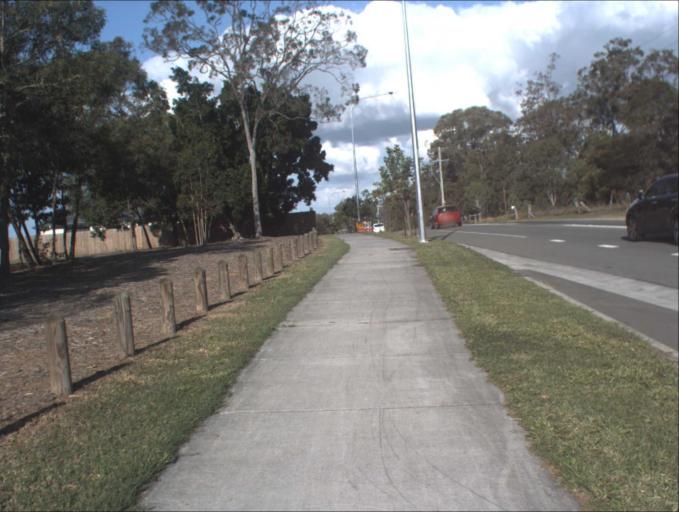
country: AU
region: Queensland
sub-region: Logan
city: Park Ridge South
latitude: -27.6885
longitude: 153.0454
